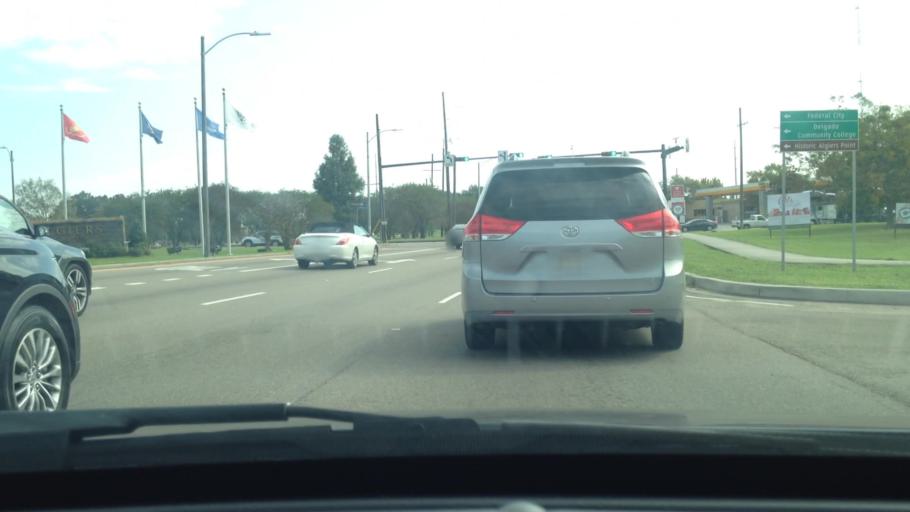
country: US
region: Louisiana
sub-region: Jefferson Parish
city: Terrytown
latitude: 29.9297
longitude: -90.0331
